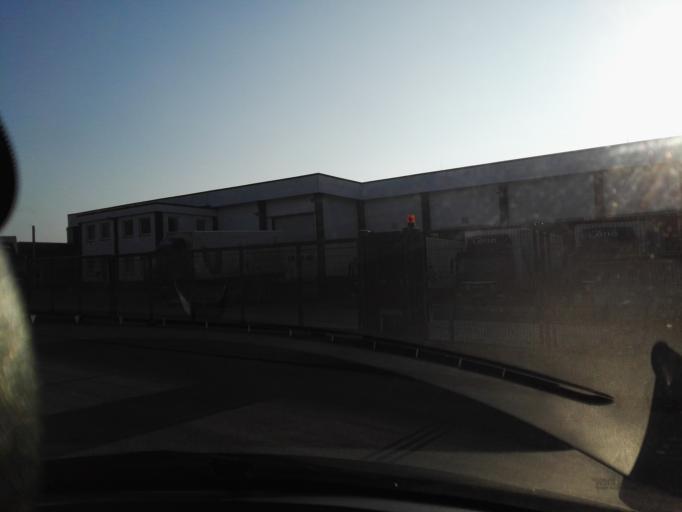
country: DE
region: Lower Saxony
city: Sarstedt
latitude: 52.2487
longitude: 9.8512
